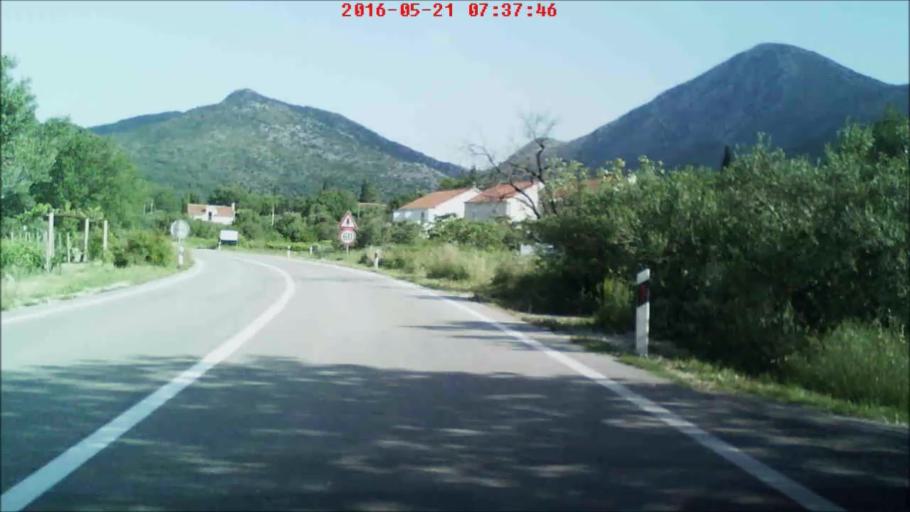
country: HR
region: Dubrovacko-Neretvanska
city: Podgora
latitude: 42.7947
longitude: 17.8545
